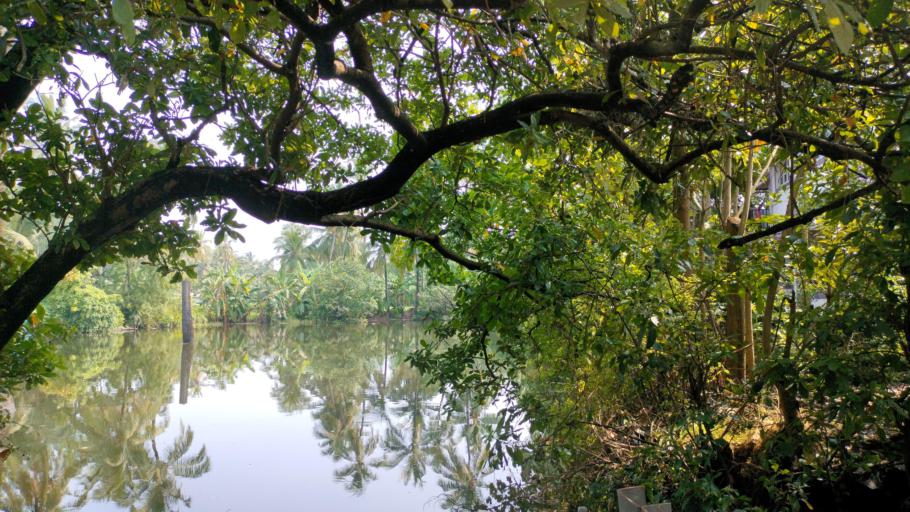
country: IN
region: Maharashtra
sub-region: Thane
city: Virar
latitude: 19.4134
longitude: 72.7866
